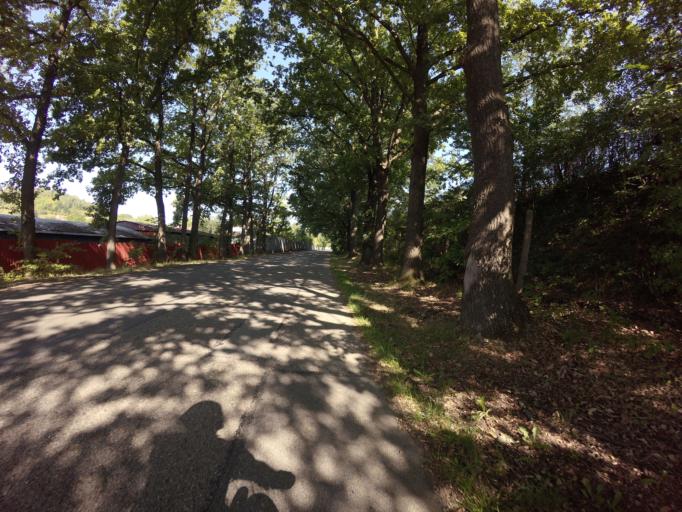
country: CZ
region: Jihocesky
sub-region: Okres Cesky Krumlov
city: Cesky Krumlov
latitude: 48.8241
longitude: 14.3137
